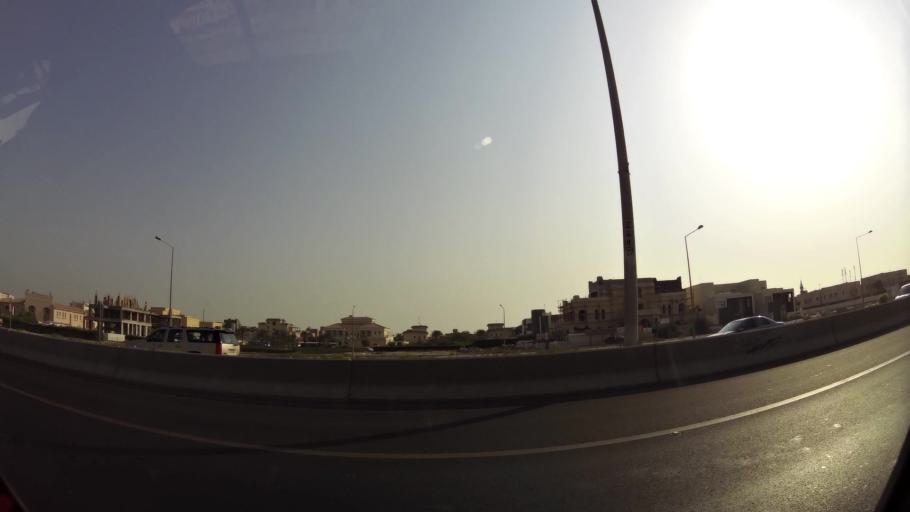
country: KW
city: Al Funaytis
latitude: 29.2360
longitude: 48.0958
